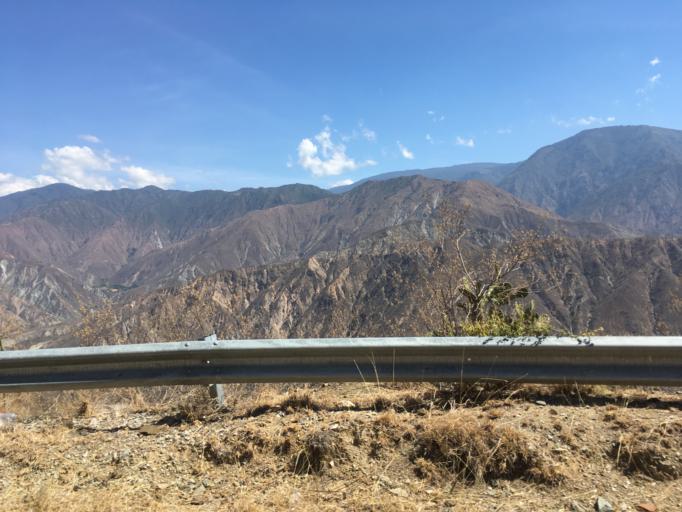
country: CO
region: Santander
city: Aratoca
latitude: 6.7812
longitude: -72.9934
